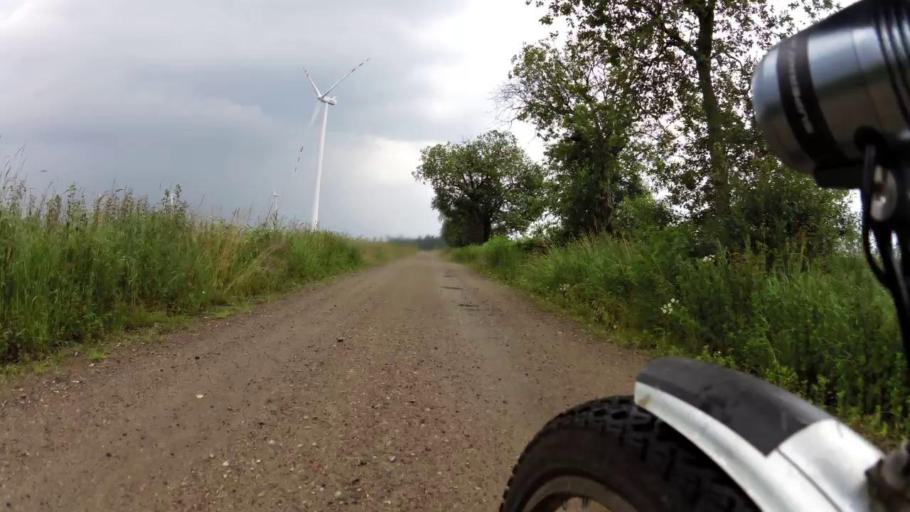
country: PL
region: West Pomeranian Voivodeship
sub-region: Powiat lobeski
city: Lobez
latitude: 53.7086
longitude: 15.6250
